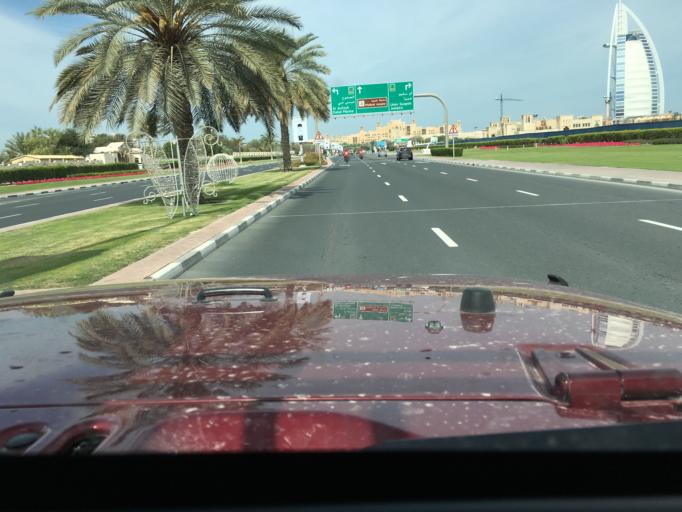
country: AE
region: Dubai
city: Dubai
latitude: 25.1303
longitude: 55.1919
